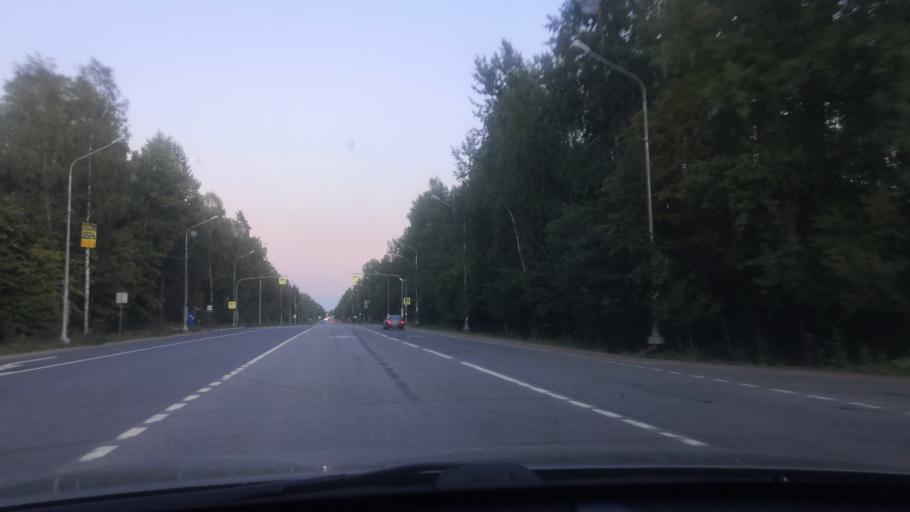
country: RU
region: St.-Petersburg
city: Pesochnyy
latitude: 60.1895
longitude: 30.0969
